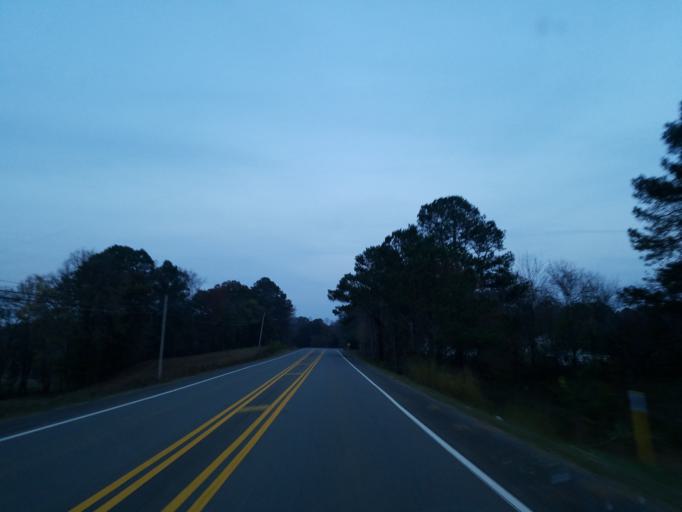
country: US
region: Georgia
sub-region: Pickens County
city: Jasper
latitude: 34.5085
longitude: -84.4986
